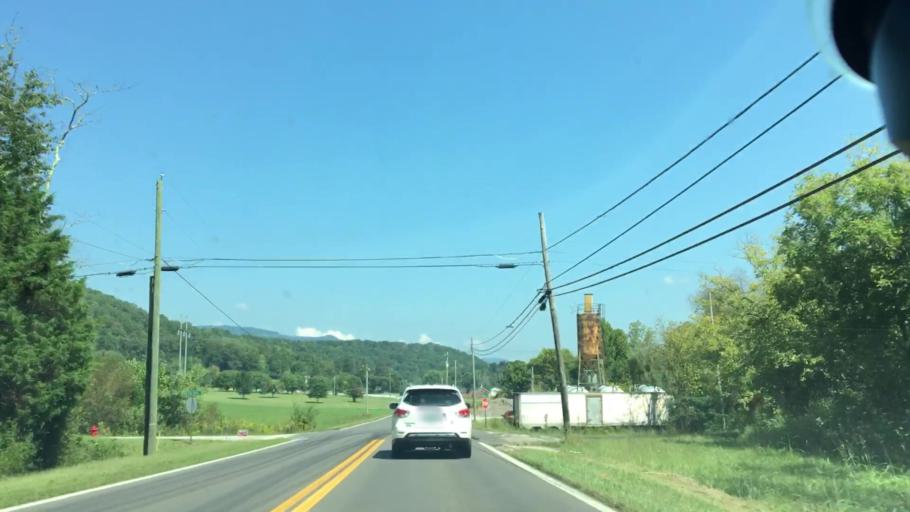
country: US
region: Tennessee
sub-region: Roane County
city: Oliver Springs
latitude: 36.0297
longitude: -84.3667
